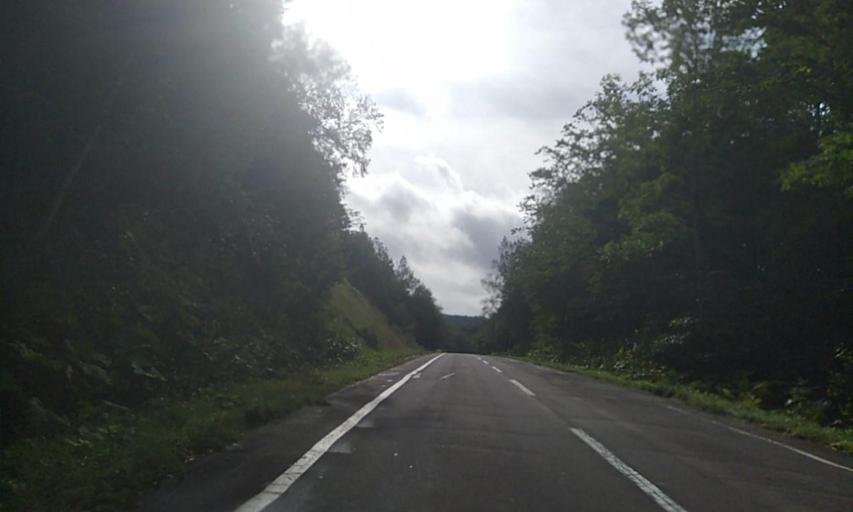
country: JP
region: Hokkaido
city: Abashiri
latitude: 43.6684
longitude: 144.5526
